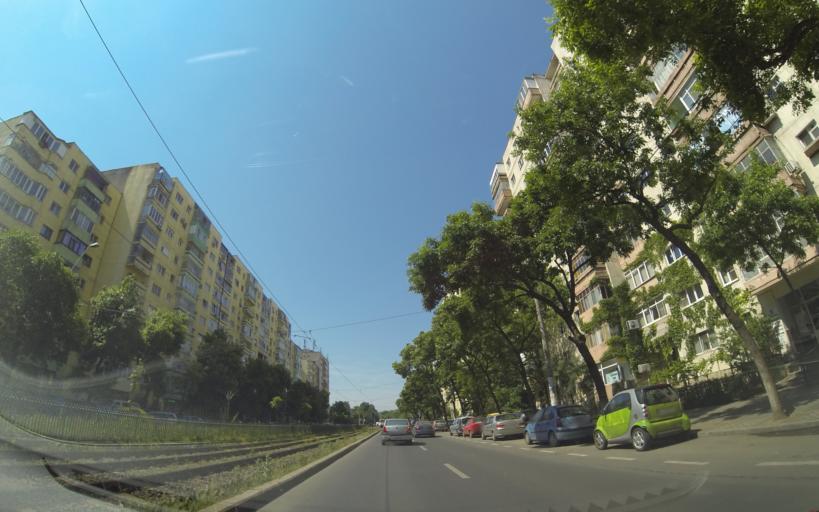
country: RO
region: Bucuresti
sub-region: Municipiul Bucuresti
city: Bucuresti
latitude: 44.4077
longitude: 26.0660
